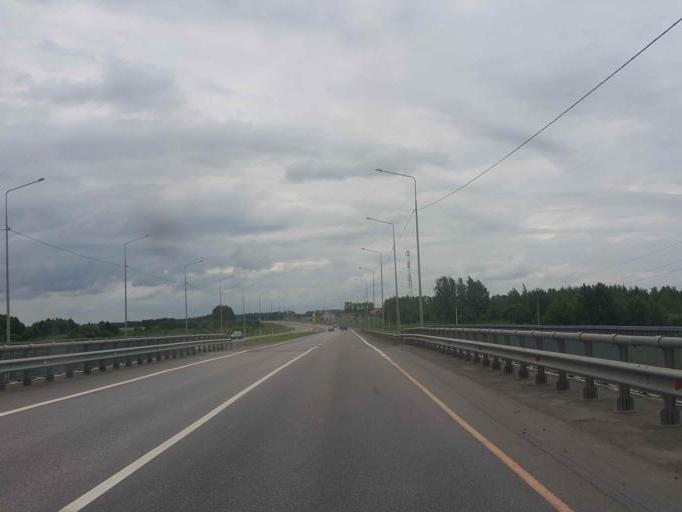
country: RU
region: Tambov
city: Zavoronezhskoye
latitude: 52.8685
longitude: 40.7593
